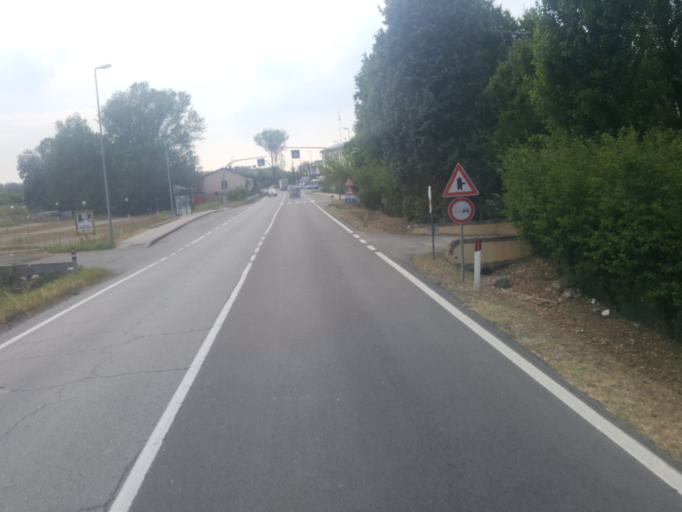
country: IT
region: Emilia-Romagna
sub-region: Provincia di Modena
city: Gaggio
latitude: 44.6226
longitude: 11.0019
